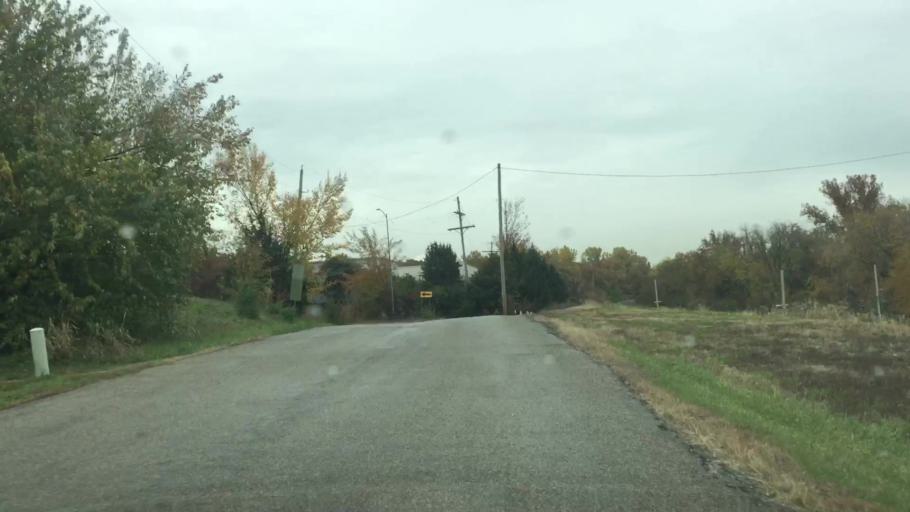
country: US
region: Kansas
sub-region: Wyandotte County
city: Edwardsville
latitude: 38.9992
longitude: -94.8230
